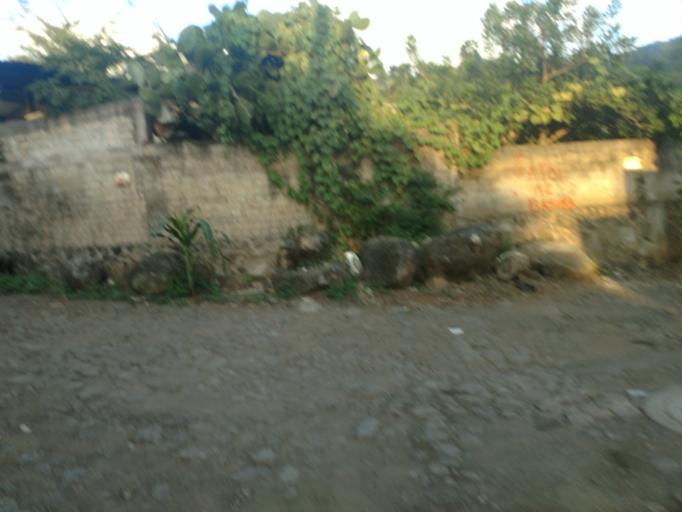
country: MX
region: Nayarit
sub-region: Tepic
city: La Corregidora
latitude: 21.4646
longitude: -104.7994
